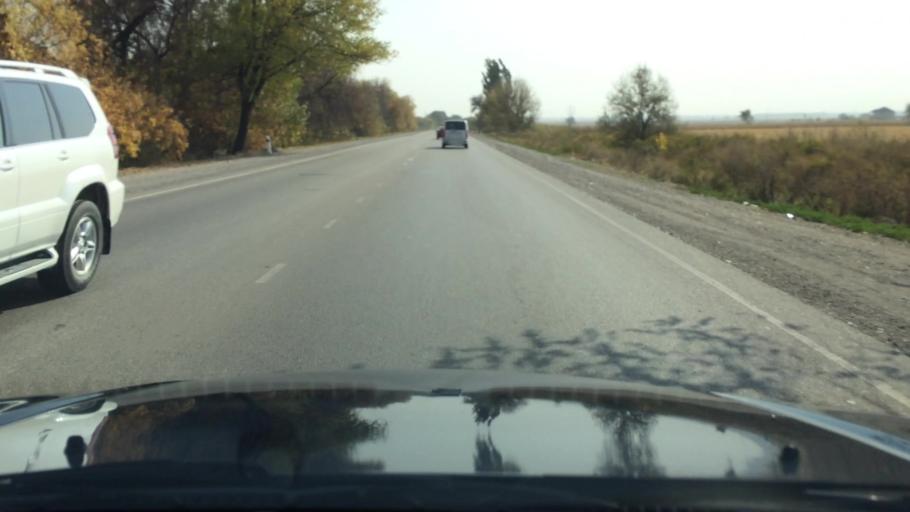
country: KG
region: Chuy
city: Lebedinovka
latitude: 42.9275
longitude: 74.6967
